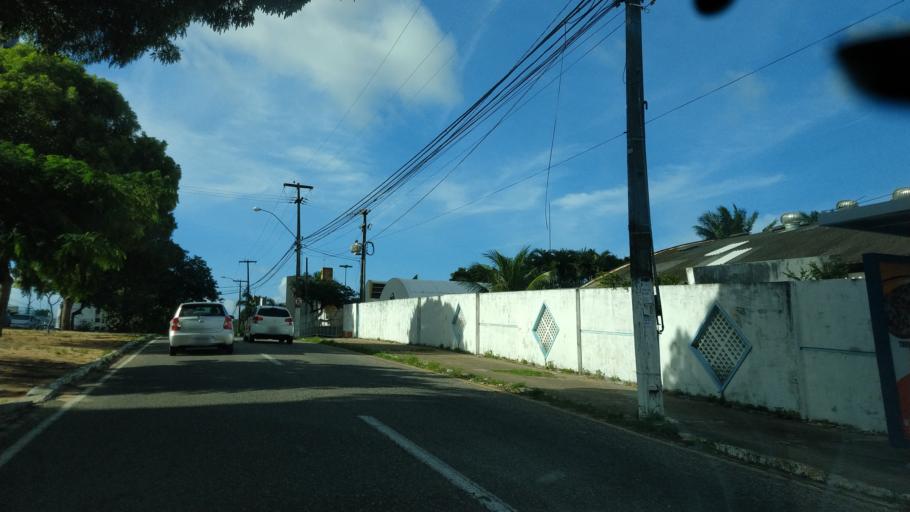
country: BR
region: Rio Grande do Norte
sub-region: Natal
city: Natal
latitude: -5.8110
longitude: -35.2012
